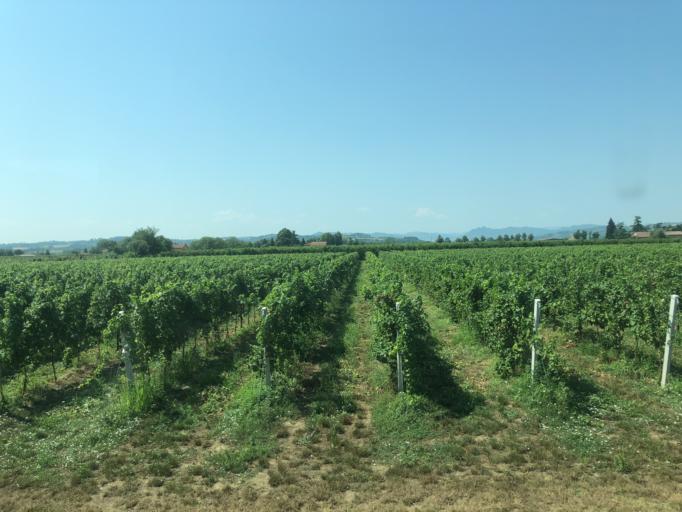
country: IT
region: Emilia-Romagna
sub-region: Provincia di Ravenna
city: Castel Bolognese
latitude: 44.3200
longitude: 11.8176
